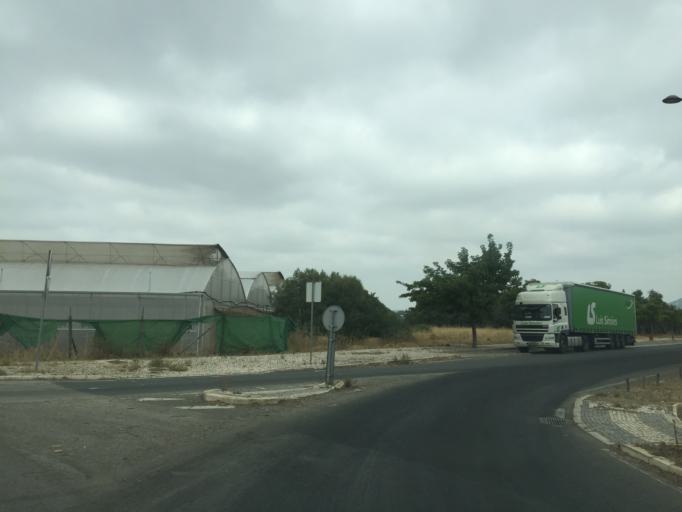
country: PT
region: Faro
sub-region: Faro
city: Santa Barbara de Nexe
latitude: 37.0782
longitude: -7.9758
